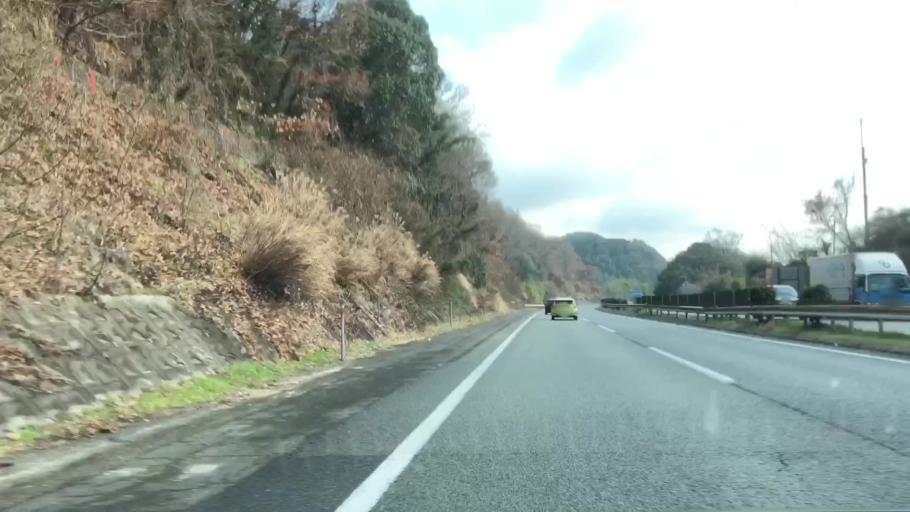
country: JP
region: Kumamoto
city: Tamana
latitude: 33.0024
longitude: 130.5865
